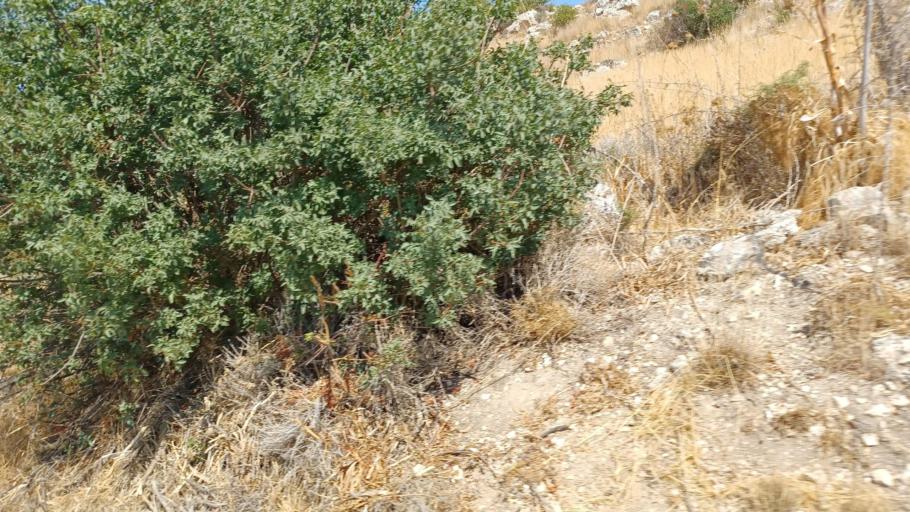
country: CY
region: Pafos
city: Polis
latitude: 34.9779
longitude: 32.4873
